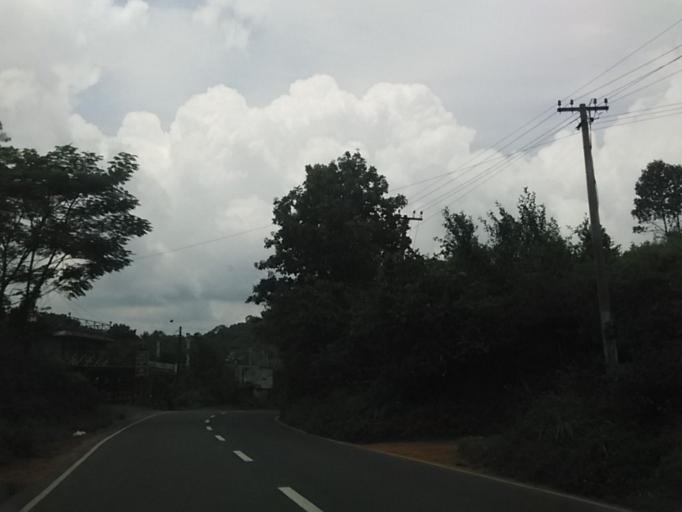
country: IN
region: Kerala
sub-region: Wayanad
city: Kalpetta
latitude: 11.5431
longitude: 76.0391
